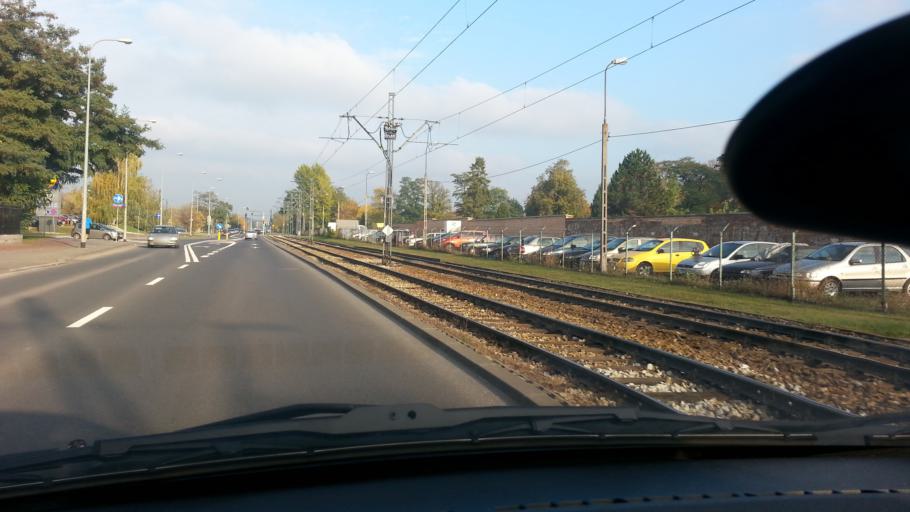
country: PL
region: Masovian Voivodeship
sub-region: Warszawa
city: Targowek
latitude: 52.2821
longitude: 21.0309
